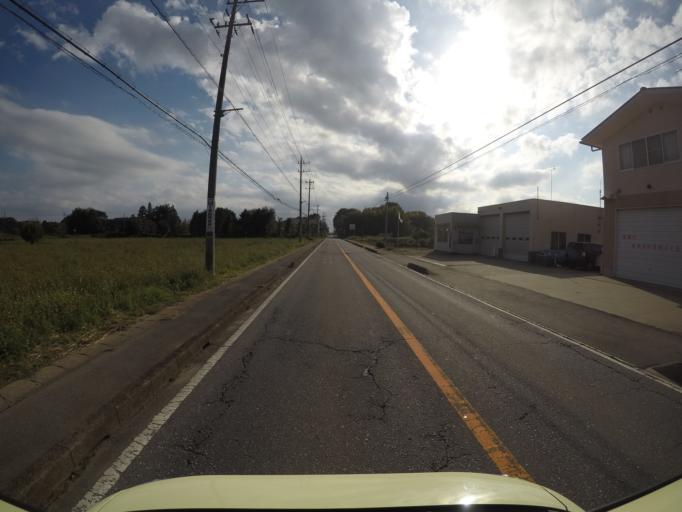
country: JP
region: Ibaraki
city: Iwai
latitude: 36.0015
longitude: 139.9049
